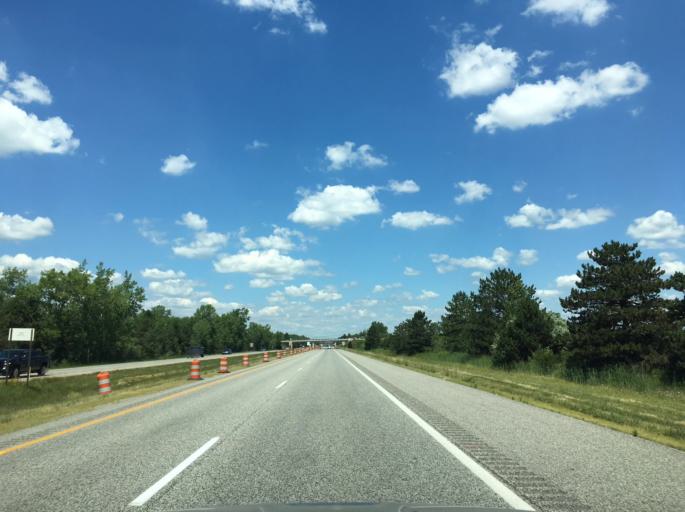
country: US
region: Michigan
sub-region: Midland County
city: Midland
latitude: 43.6228
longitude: -84.1740
